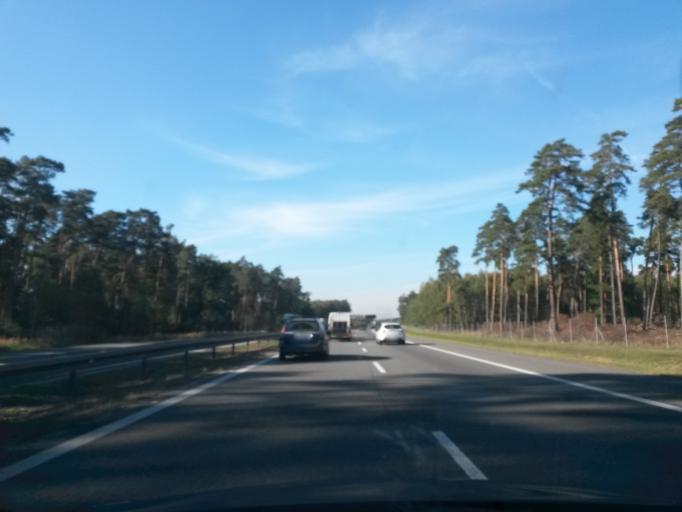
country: PL
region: Opole Voivodeship
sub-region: Powiat opolski
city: Proszkow
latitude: 50.5367
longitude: 17.9041
